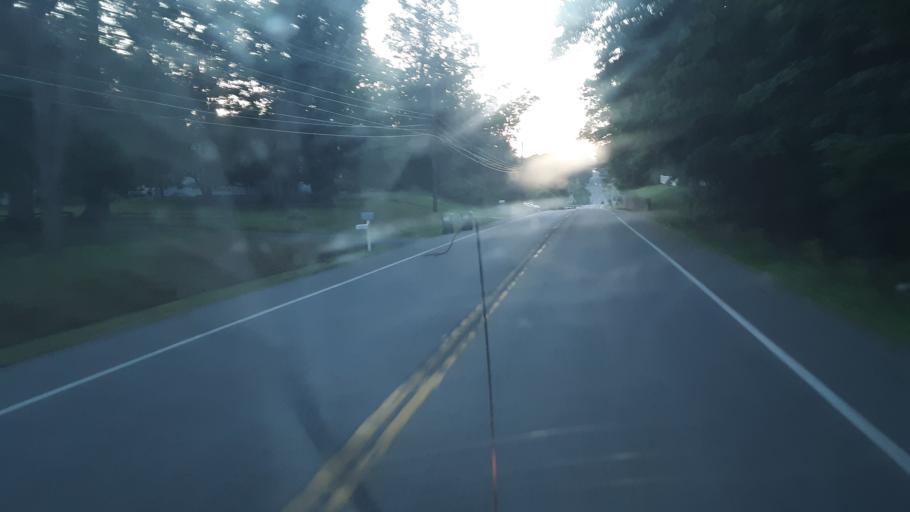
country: US
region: New York
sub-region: Saratoga County
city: Ballston Spa
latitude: 42.9997
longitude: -73.8629
